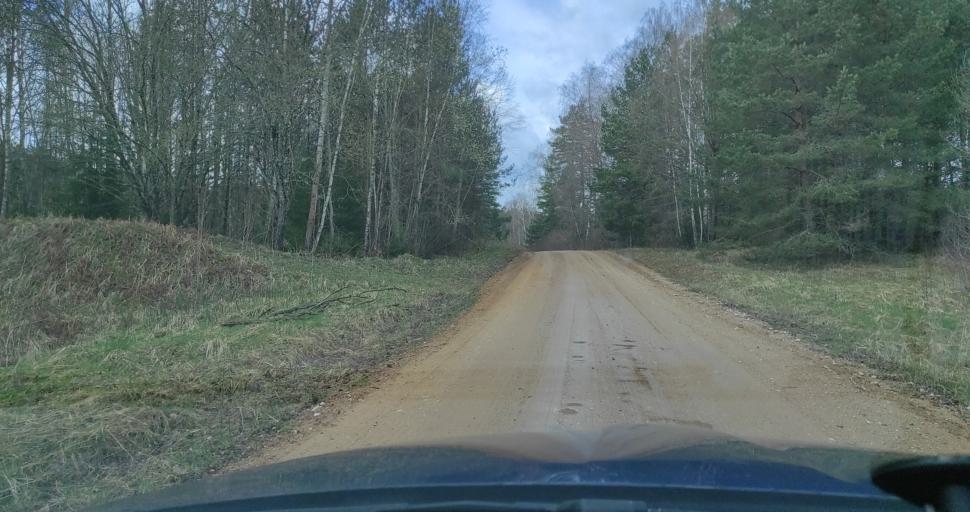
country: LV
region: Kuldigas Rajons
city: Kuldiga
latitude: 57.0576
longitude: 21.8069
